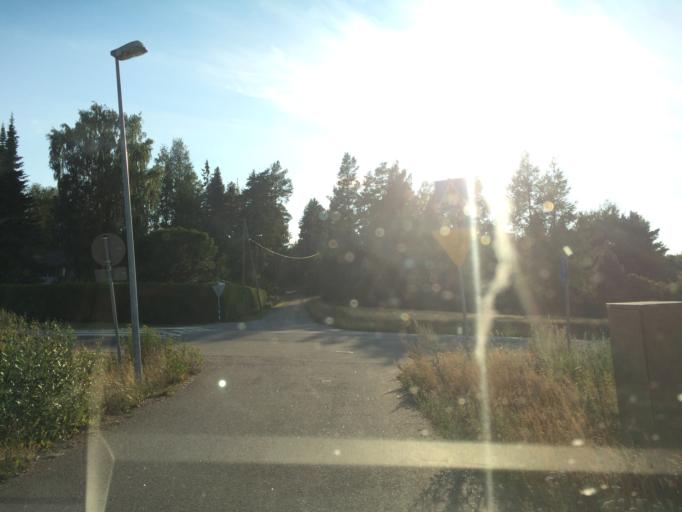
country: FI
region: Haeme
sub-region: Haemeenlinna
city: Parola
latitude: 61.0462
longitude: 24.3780
